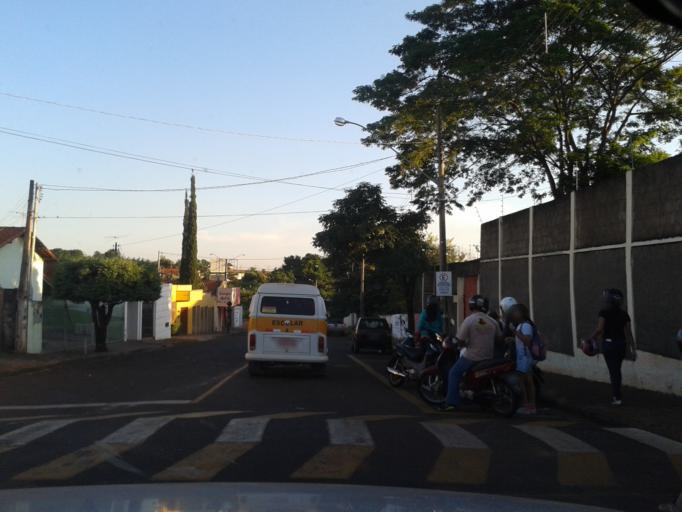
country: BR
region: Minas Gerais
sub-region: Ituiutaba
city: Ituiutaba
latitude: -18.9774
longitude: -49.4691
